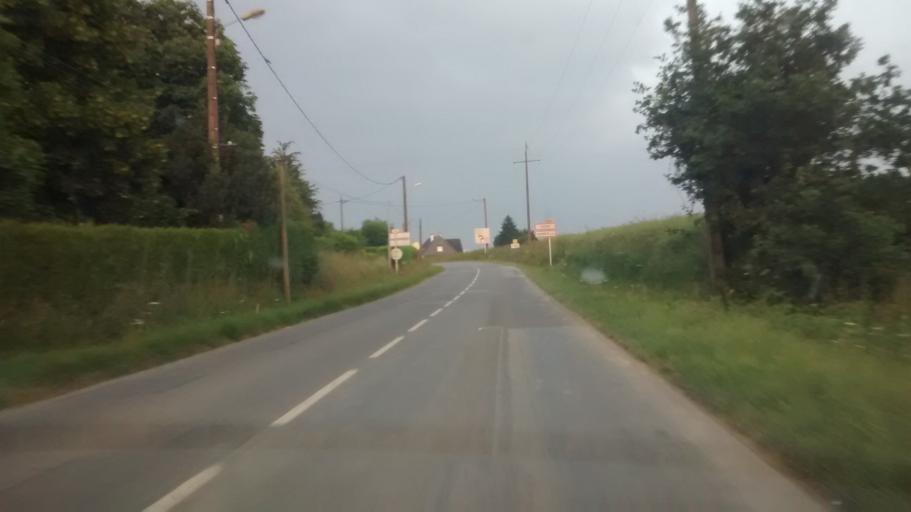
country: FR
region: Brittany
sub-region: Departement du Morbihan
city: Guer
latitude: 47.9025
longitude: -2.1258
